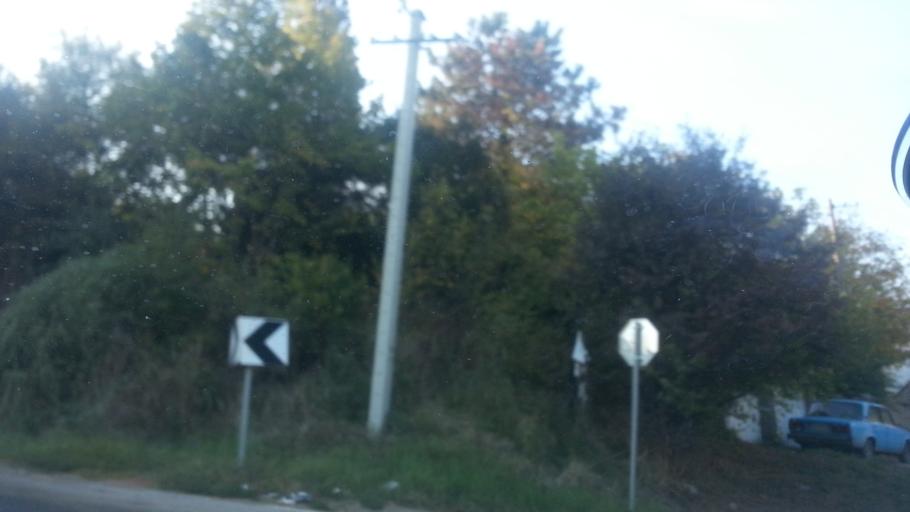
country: RS
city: Novi Slankamen
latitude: 45.1427
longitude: 20.2550
